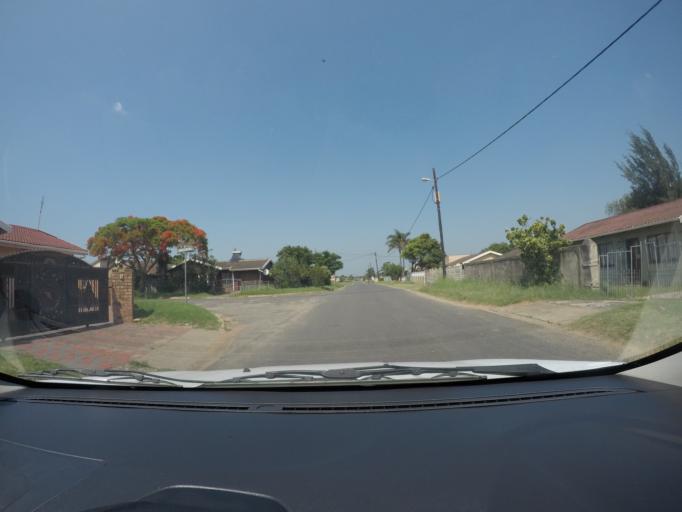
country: ZA
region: KwaZulu-Natal
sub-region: uThungulu District Municipality
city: eSikhawini
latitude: -28.8607
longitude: 31.9184
